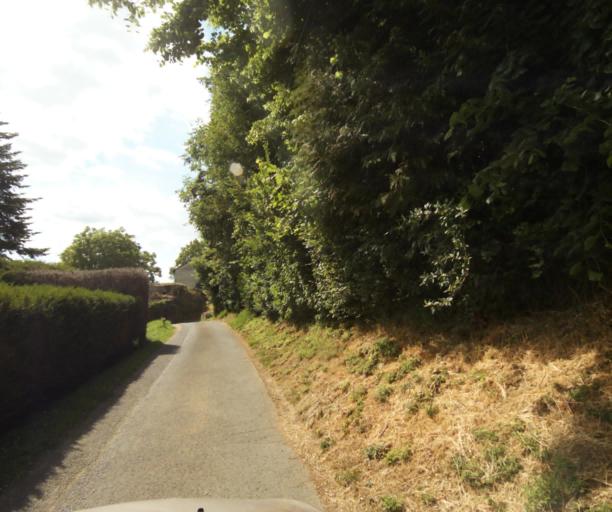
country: FR
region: Champagne-Ardenne
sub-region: Departement des Ardennes
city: Montcy-Notre-Dame
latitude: 49.7588
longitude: 4.7432
